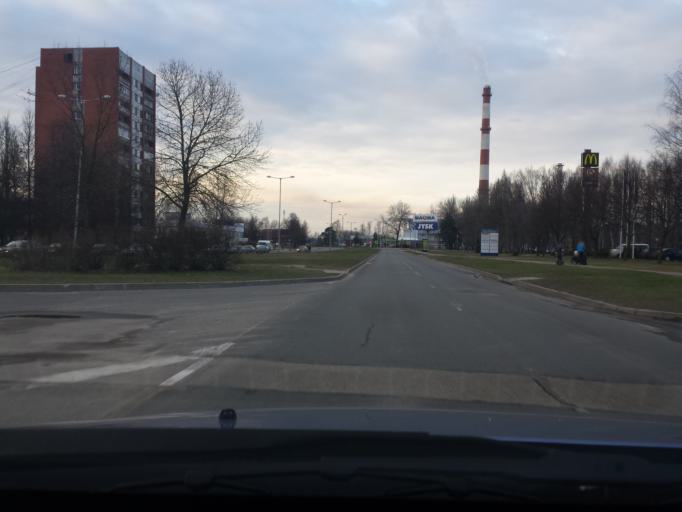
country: LV
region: Marupe
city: Marupe
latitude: 56.9583
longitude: 24.0352
